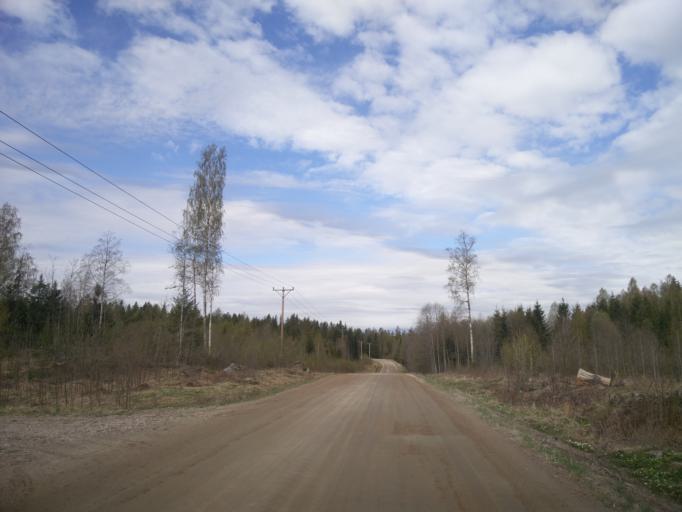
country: SE
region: Vaesternorrland
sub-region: Sundsvalls Kommun
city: Vi
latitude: 62.2758
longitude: 17.2151
